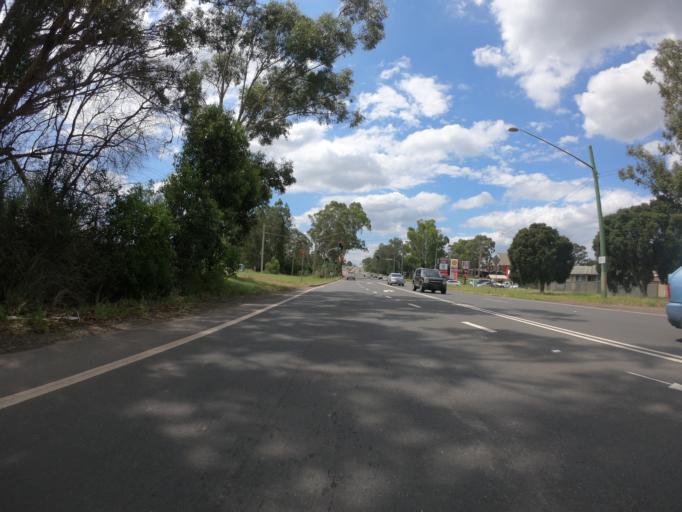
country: AU
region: New South Wales
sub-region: Blacktown
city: Mount Druitt
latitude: -33.7889
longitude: 150.7702
